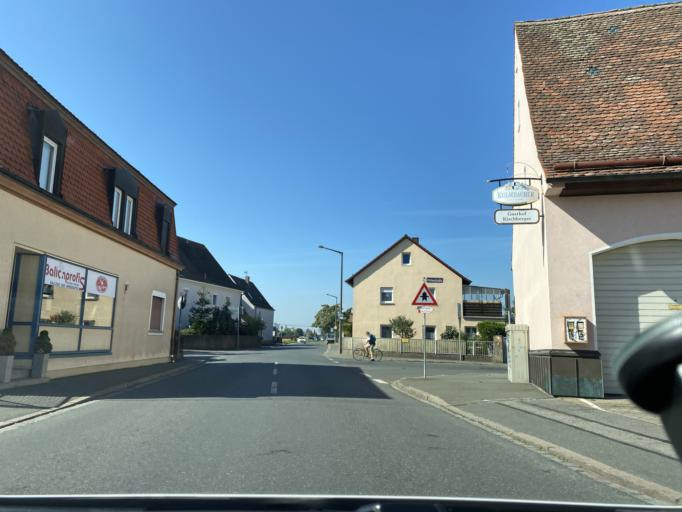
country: DE
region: Bavaria
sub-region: Regierungsbezirk Mittelfranken
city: Furth
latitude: 49.5011
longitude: 11.0119
